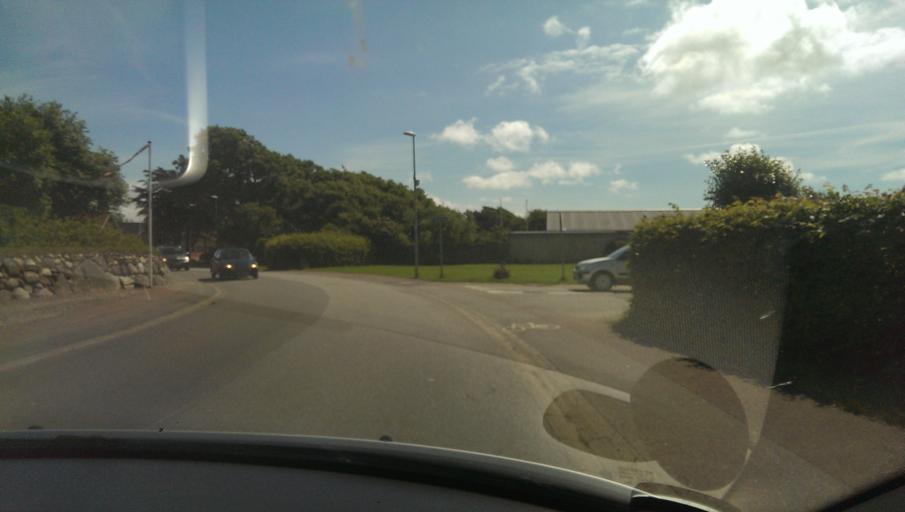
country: DK
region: Central Jutland
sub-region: Ringkobing-Skjern Kommune
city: Ringkobing
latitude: 56.1271
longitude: 8.1774
